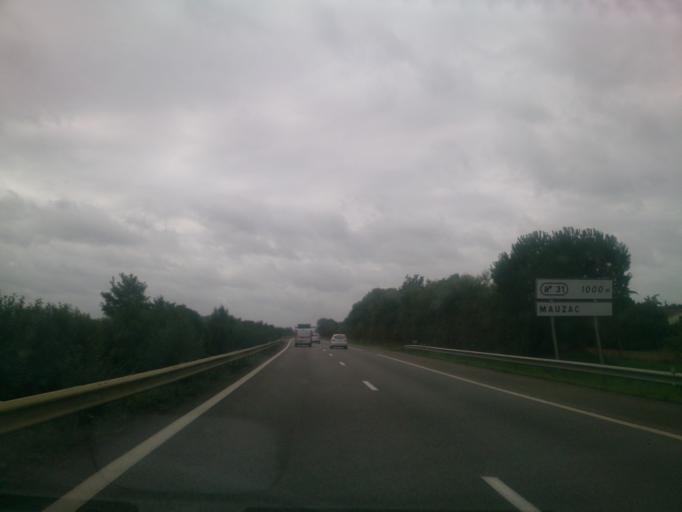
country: FR
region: Midi-Pyrenees
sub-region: Departement de la Haute-Garonne
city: Le Fauga
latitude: 43.3967
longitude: 1.2882
